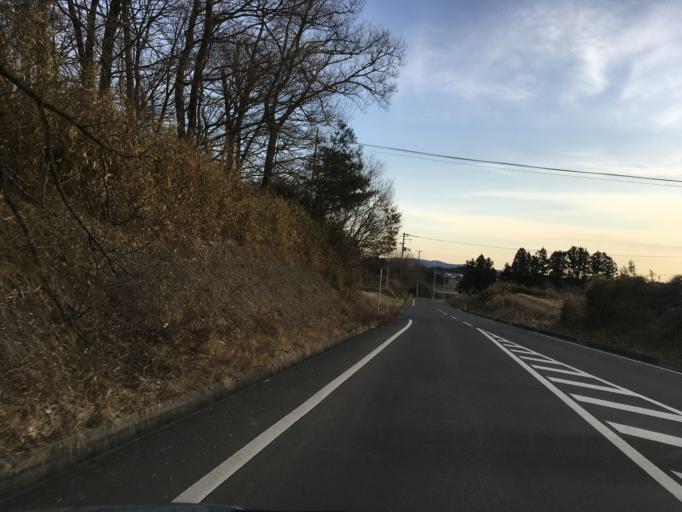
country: JP
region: Miyagi
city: Kogota
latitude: 38.6935
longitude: 141.0954
